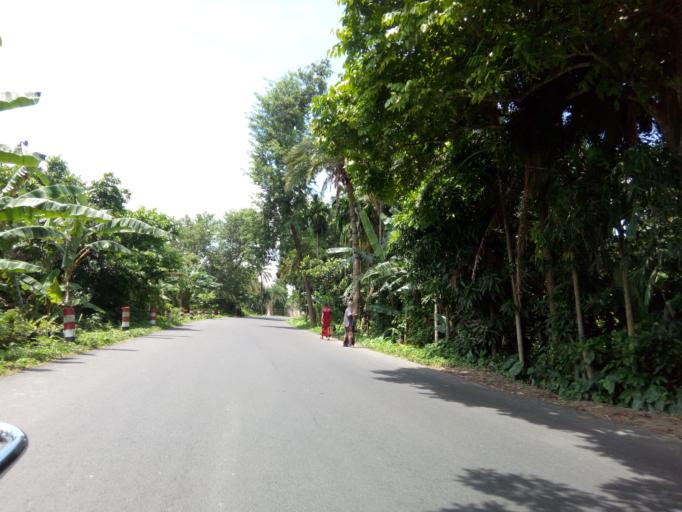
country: BD
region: Dhaka
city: Tungipara
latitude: 22.9103
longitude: 89.8685
